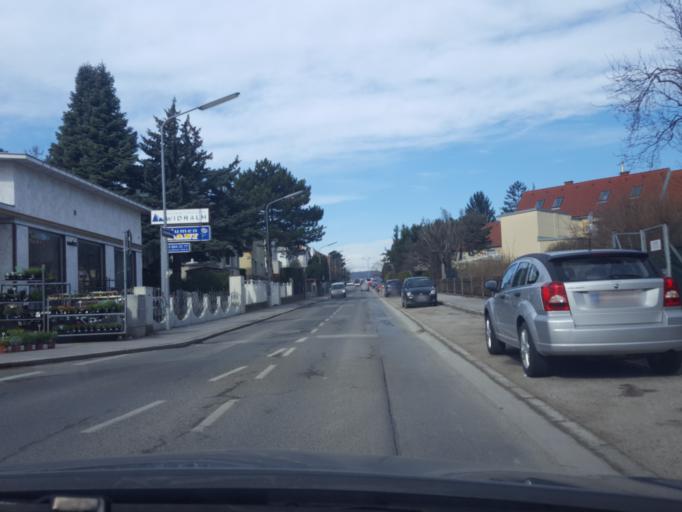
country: AT
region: Lower Austria
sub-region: Politischer Bezirk Modling
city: Perchtoldsdorf
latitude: 48.1619
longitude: 16.2960
